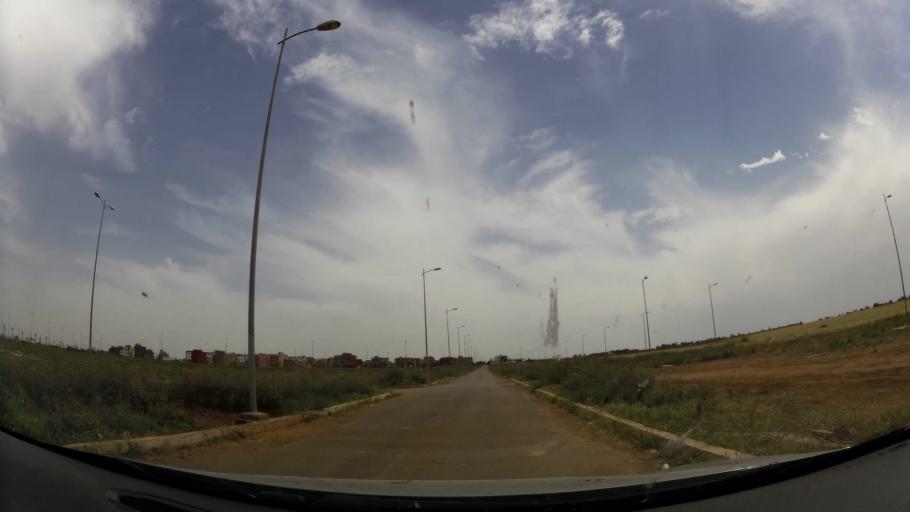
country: MA
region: Rabat-Sale-Zemmour-Zaer
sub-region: Khemisset
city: Khemisset
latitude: 33.8191
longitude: -6.0922
